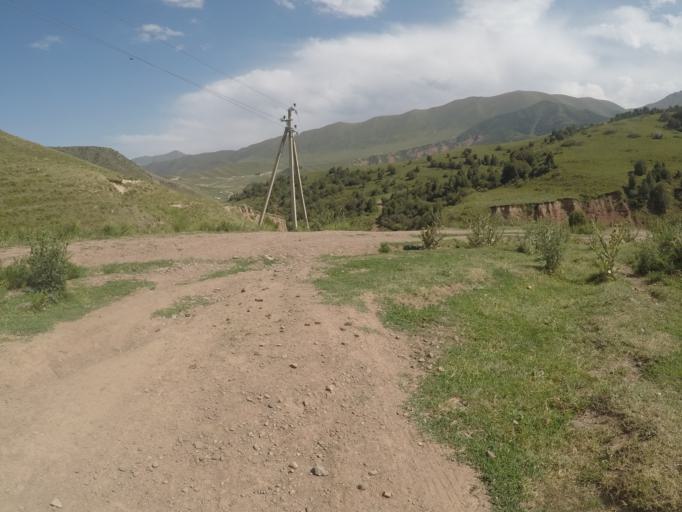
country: KG
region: Chuy
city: Bishkek
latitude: 42.6437
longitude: 74.6037
